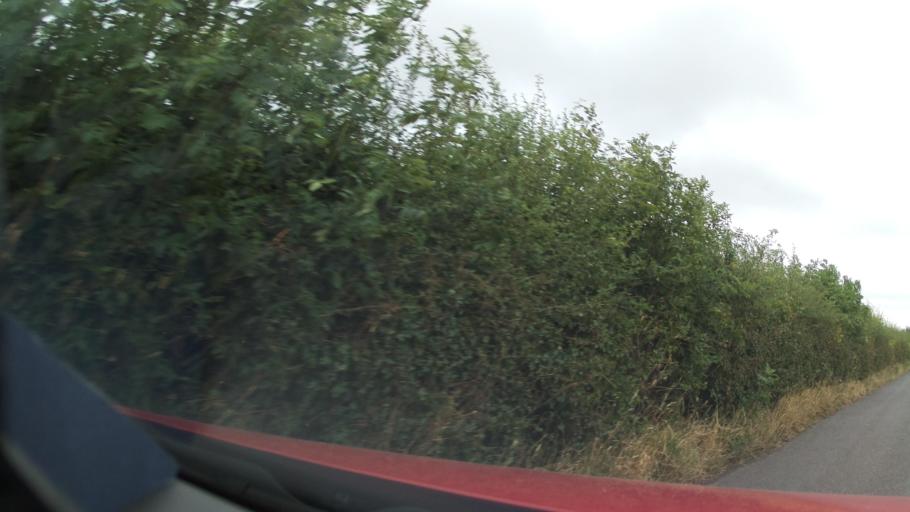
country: GB
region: England
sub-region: Leicestershire
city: Ashby de la Zouch
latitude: 52.7753
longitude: -1.5064
